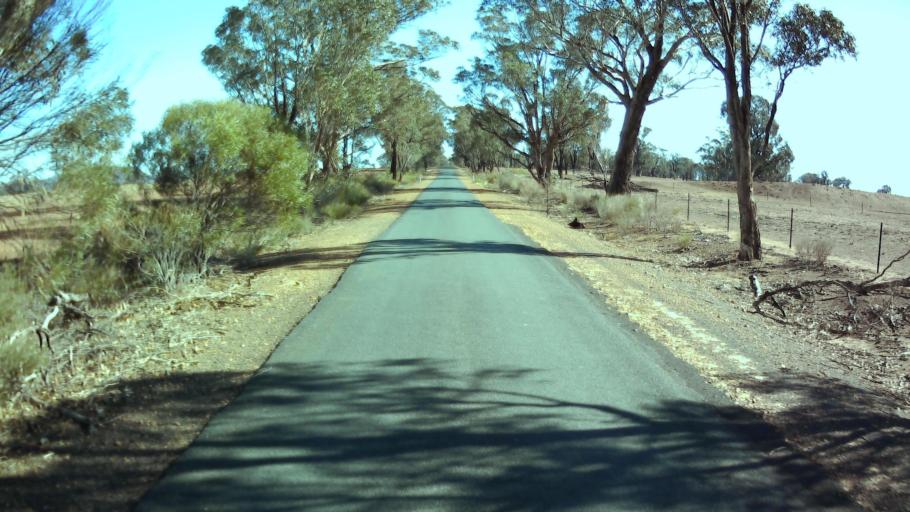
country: AU
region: New South Wales
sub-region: Weddin
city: Grenfell
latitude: -33.7901
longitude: 147.9576
